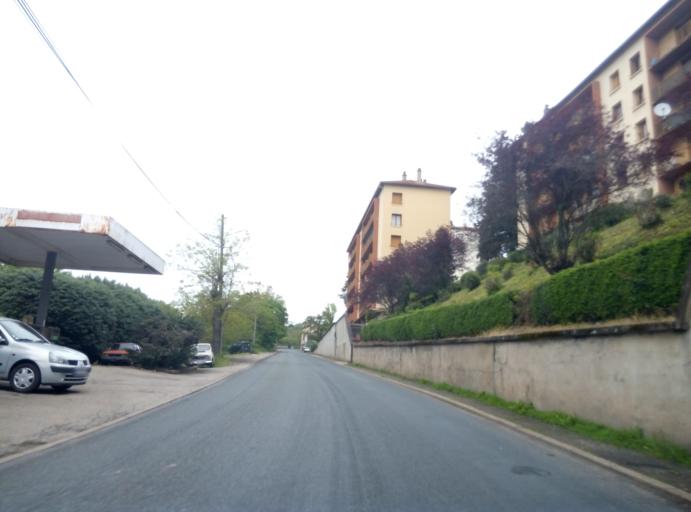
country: FR
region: Rhone-Alpes
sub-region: Departement du Rhone
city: Tarare
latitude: 45.9024
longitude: 4.4327
